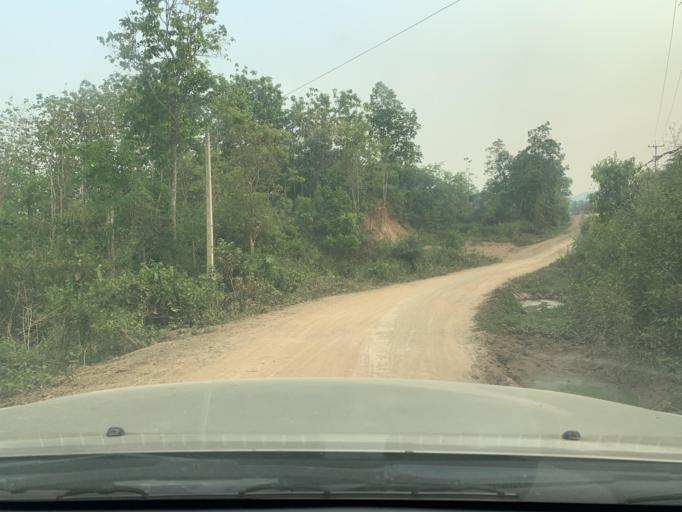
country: LA
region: Louangphabang
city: Louangphabang
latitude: 19.9198
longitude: 102.0757
